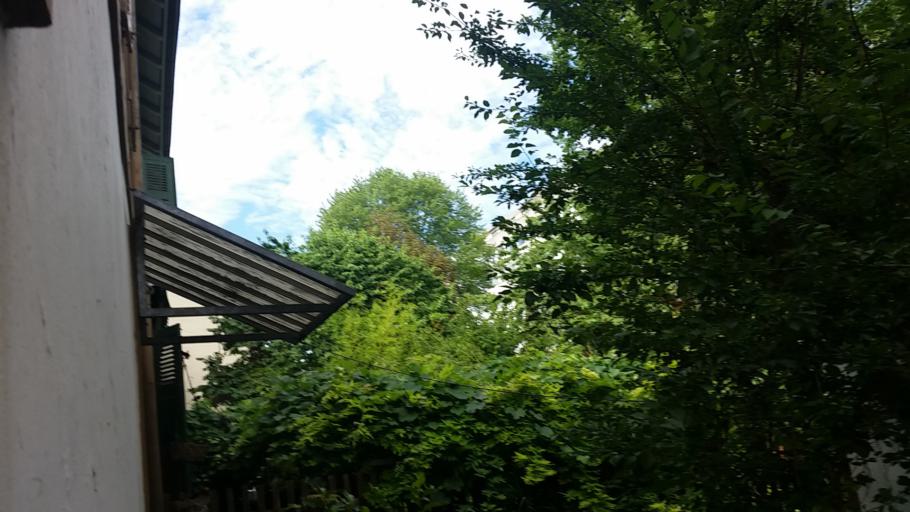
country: CH
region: Basel-City
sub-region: Basel-Stadt
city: Basel
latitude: 47.5669
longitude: 7.5639
